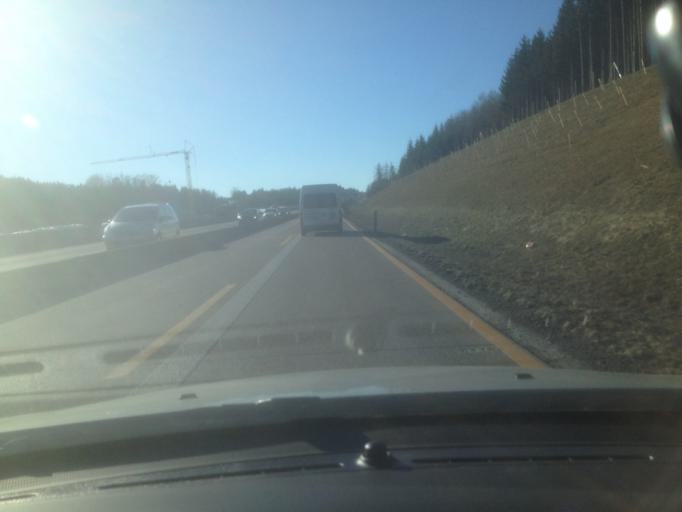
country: DE
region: Bavaria
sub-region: Swabia
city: Aystetten
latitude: 48.4191
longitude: 10.7748
